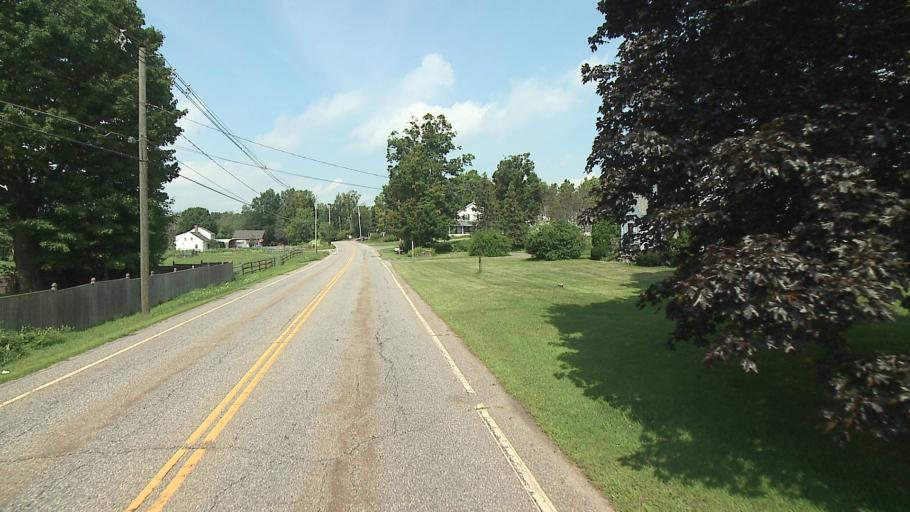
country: US
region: Connecticut
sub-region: Litchfield County
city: Bethlehem Village
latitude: 41.6853
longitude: -73.1713
